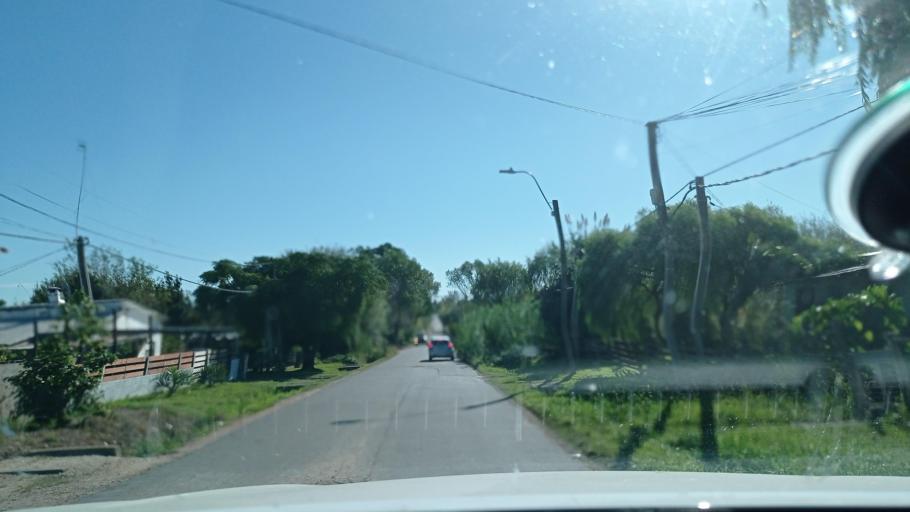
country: UY
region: Canelones
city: Joaquin Suarez
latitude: -34.7557
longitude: -55.9939
